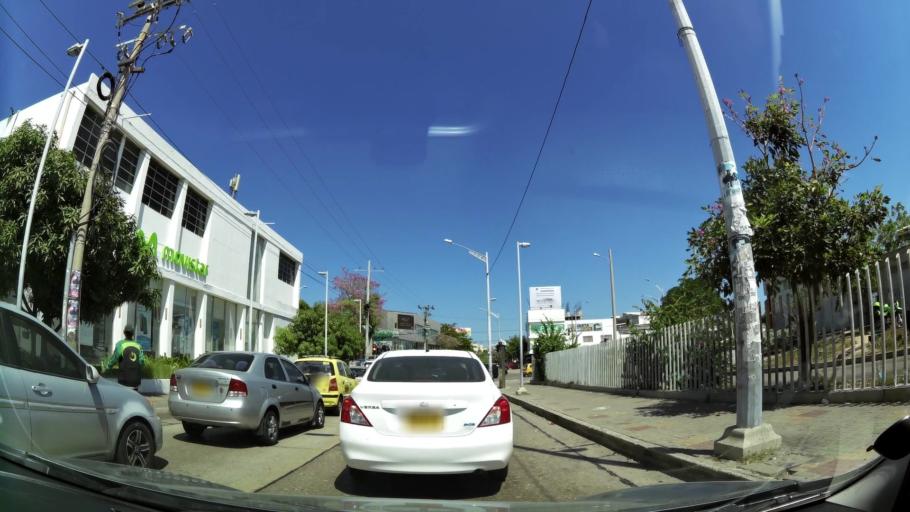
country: CO
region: Atlantico
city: Barranquilla
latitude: 10.9951
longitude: -74.8081
